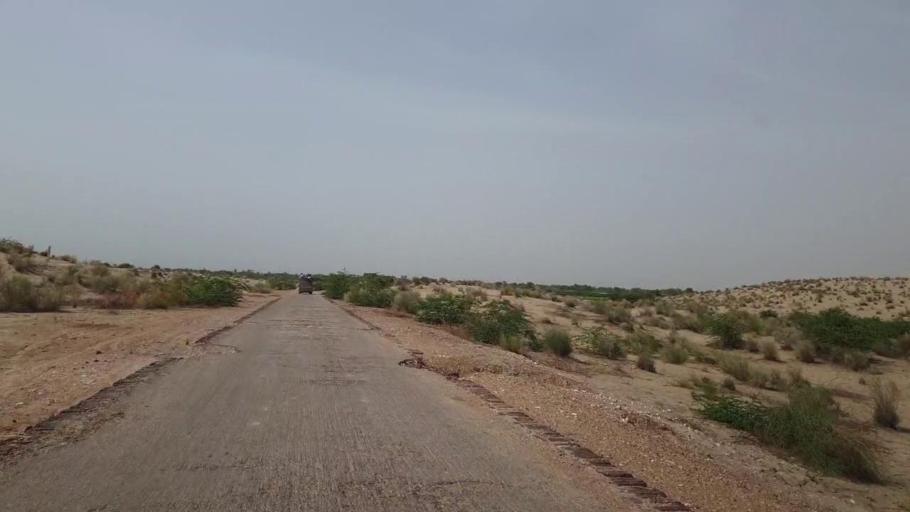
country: PK
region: Sindh
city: Bandhi
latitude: 26.5590
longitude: 68.3822
